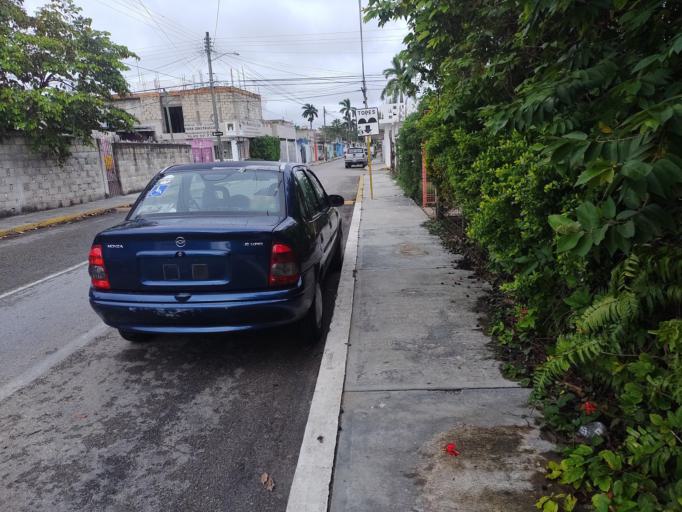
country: MX
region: Quintana Roo
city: San Miguel de Cozumel
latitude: 20.5039
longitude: -86.9494
